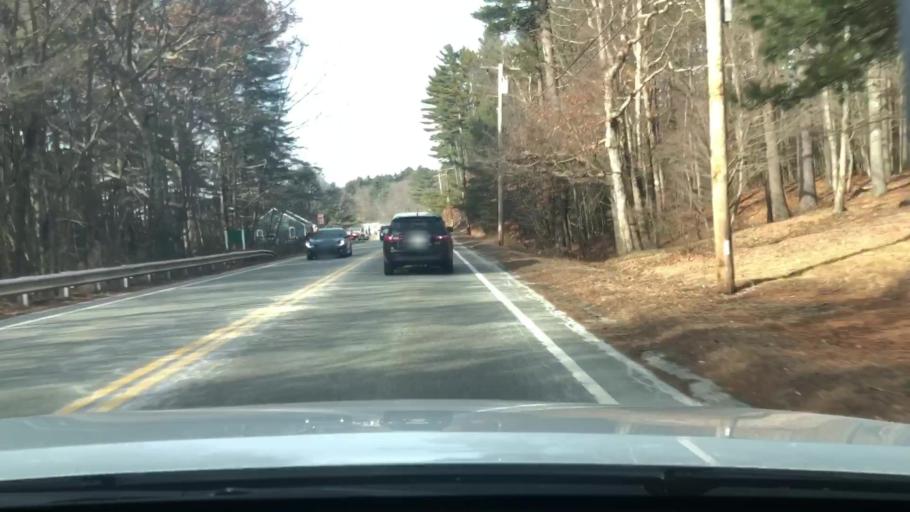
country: US
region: Massachusetts
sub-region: Worcester County
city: Northbridge
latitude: 42.1780
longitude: -71.6386
